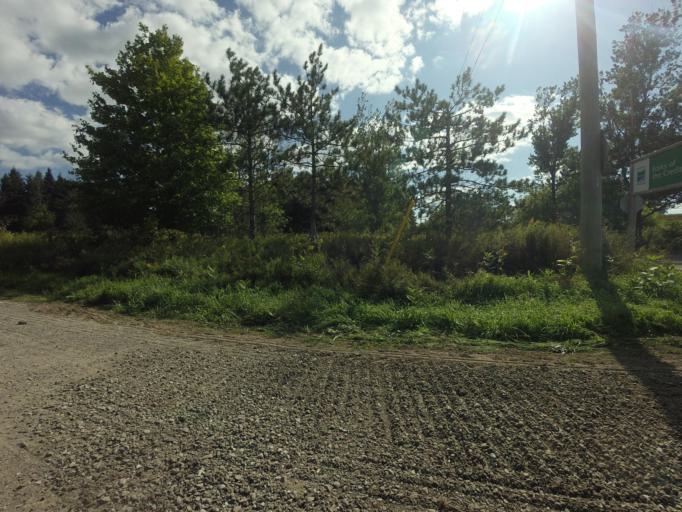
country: CA
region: Ontario
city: Orangeville
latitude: 43.8286
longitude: -80.0015
